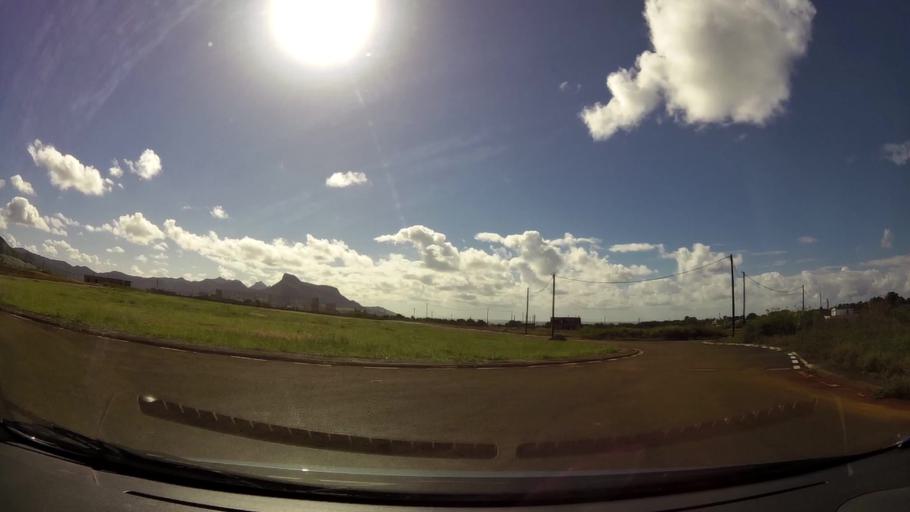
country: MU
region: Grand Port
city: Mahebourg
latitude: -20.4065
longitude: 57.6906
